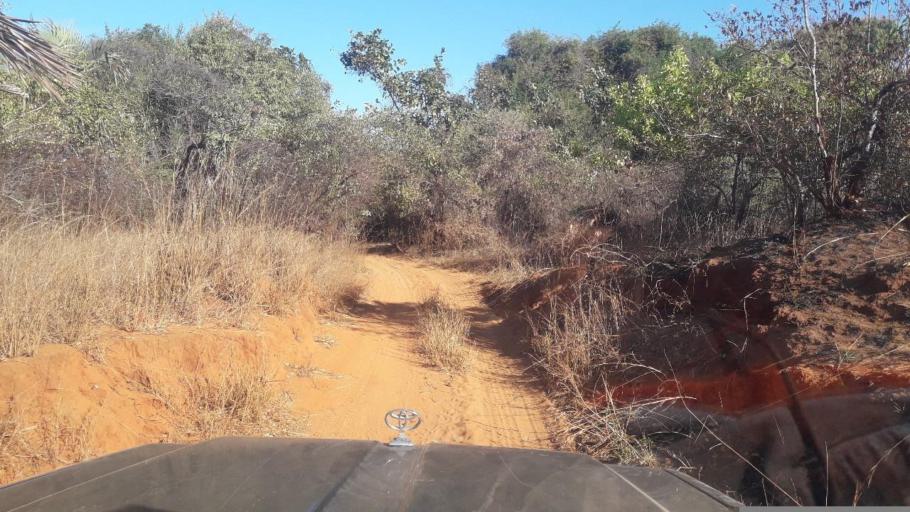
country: MG
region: Boeny
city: Sitampiky
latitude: -16.4095
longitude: 45.6012
